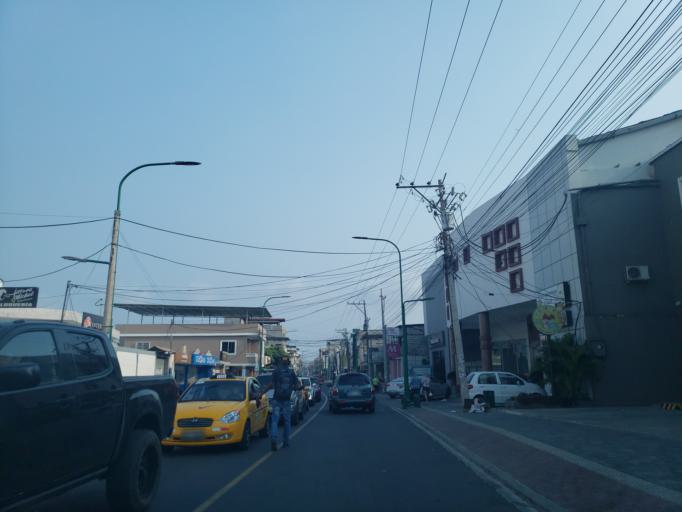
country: EC
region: Manabi
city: Manta
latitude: -0.9452
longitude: -80.7345
